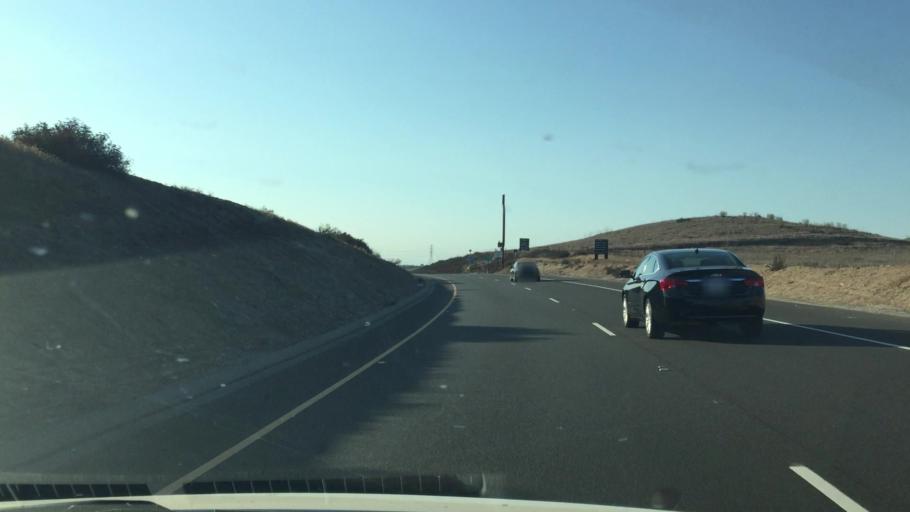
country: US
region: California
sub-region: Orange County
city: Laguna Woods
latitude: 33.6243
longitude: -117.7563
